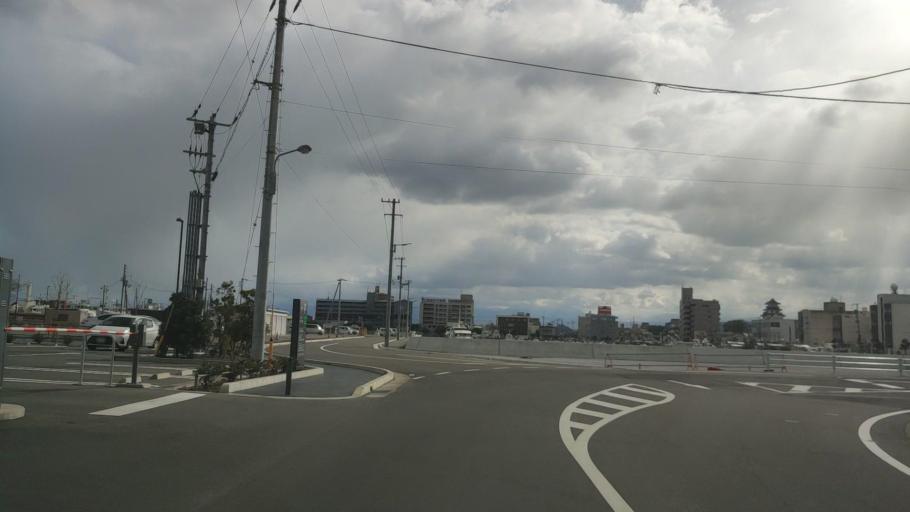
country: JP
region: Ehime
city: Saijo
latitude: 34.0692
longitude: 133.0052
